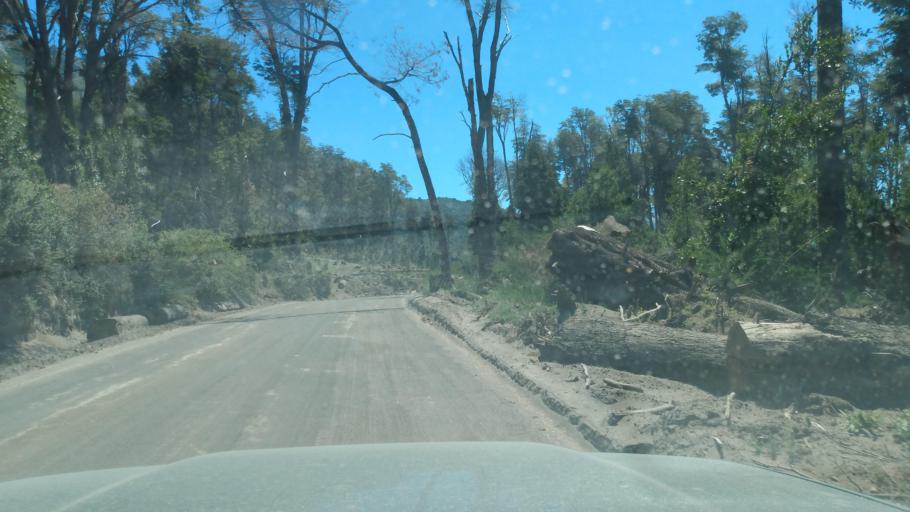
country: AR
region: Neuquen
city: Villa La Angostura
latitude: -40.6488
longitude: -71.4338
